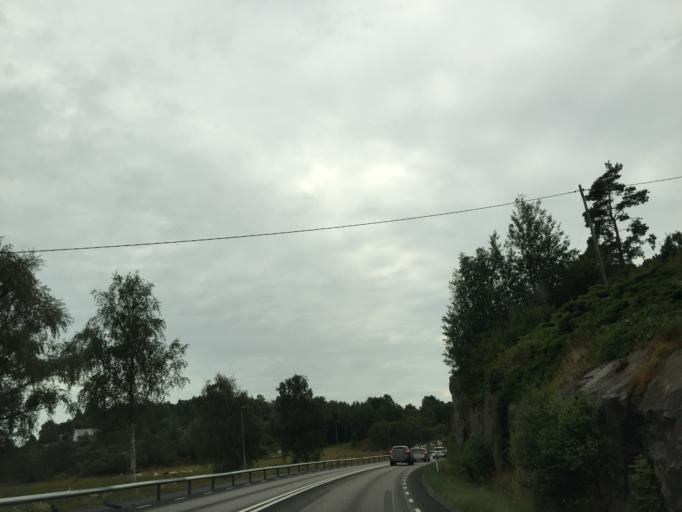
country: SE
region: Vaestra Goetaland
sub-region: Tjorns Kommun
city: Myggenas
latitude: 58.0497
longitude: 11.7553
